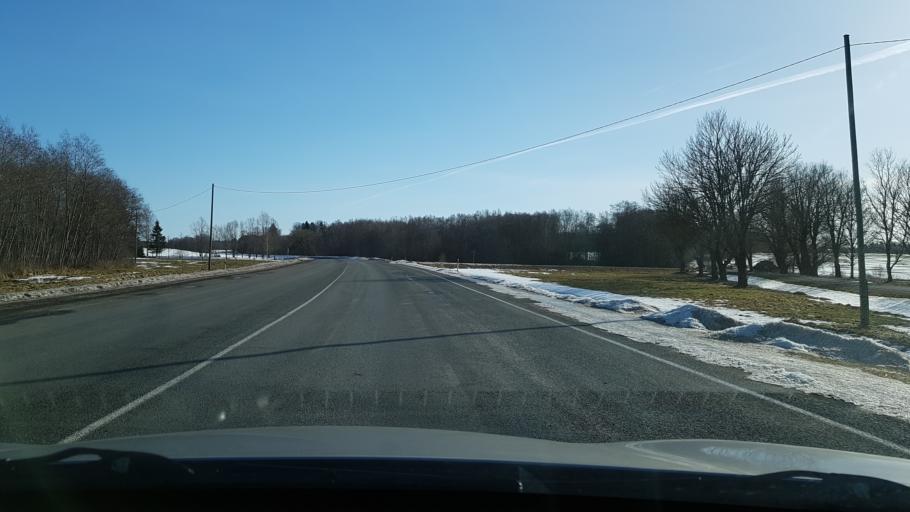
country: EE
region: Viljandimaa
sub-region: Suure-Jaani vald
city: Suure-Jaani
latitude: 58.5505
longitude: 25.4546
